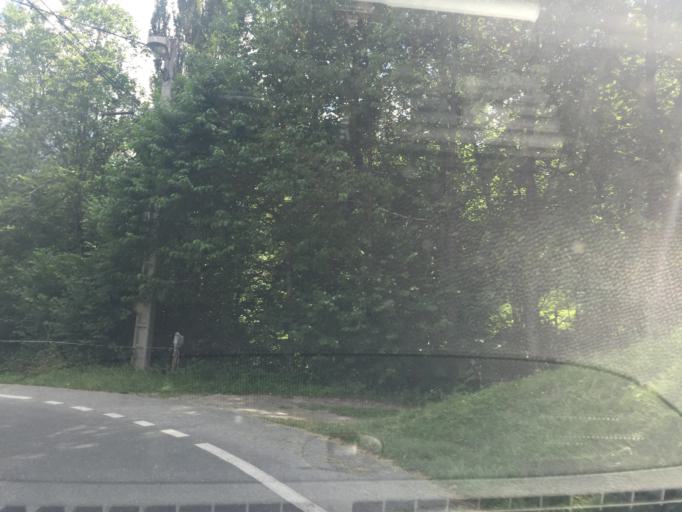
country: FR
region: Rhone-Alpes
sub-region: Departement de la Savoie
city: Bourg-Saint-Maurice
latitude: 45.6182
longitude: 6.7618
